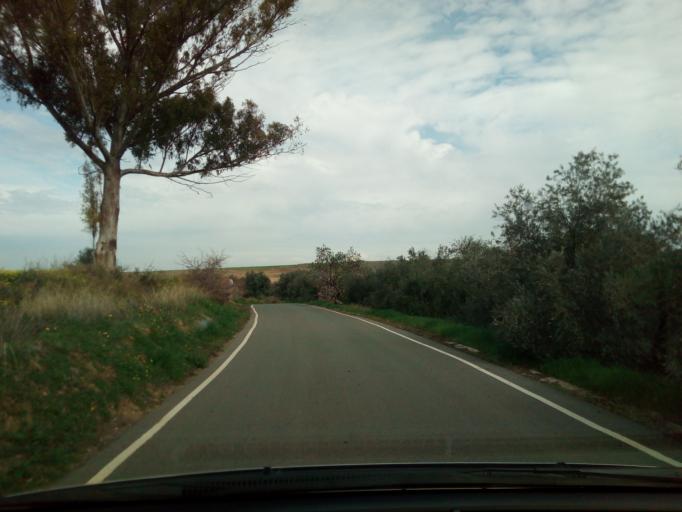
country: CY
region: Lefkosia
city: Astromeritis
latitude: 35.0873
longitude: 32.9947
